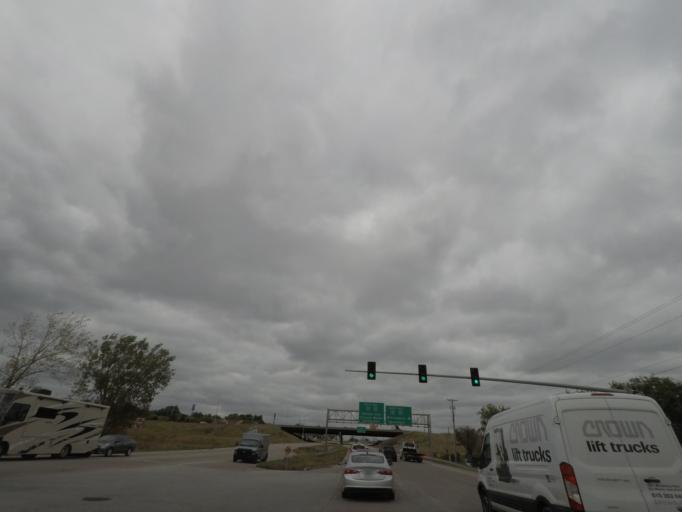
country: US
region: Iowa
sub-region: Polk County
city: Saylorville
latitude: 41.6476
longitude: -93.6004
